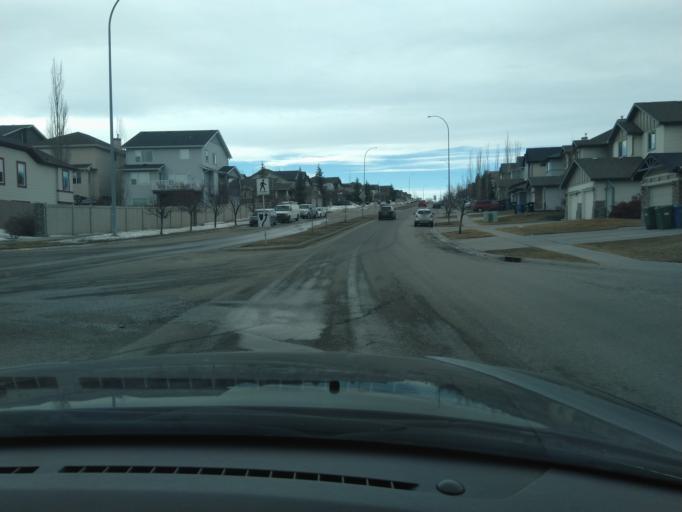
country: CA
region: Alberta
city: Calgary
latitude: 51.1632
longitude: -114.0802
